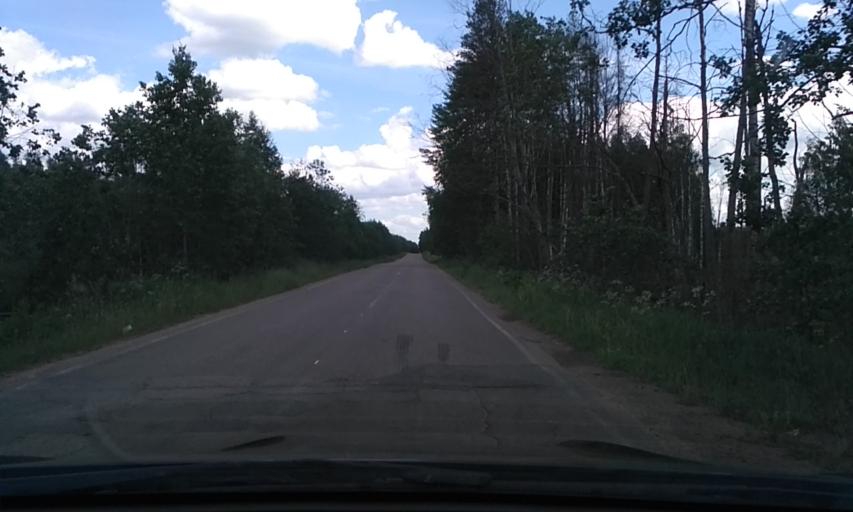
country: RU
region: Leningrad
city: Otradnoye
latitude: 59.8196
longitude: 30.8162
